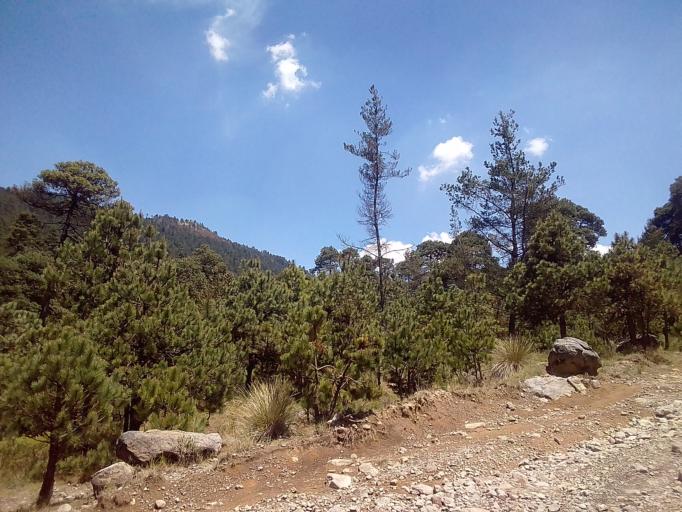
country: MX
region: Mexico City
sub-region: Cuajimalpa de Morelos
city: San Lorenzo Acopilco
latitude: 19.2849
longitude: -99.3328
